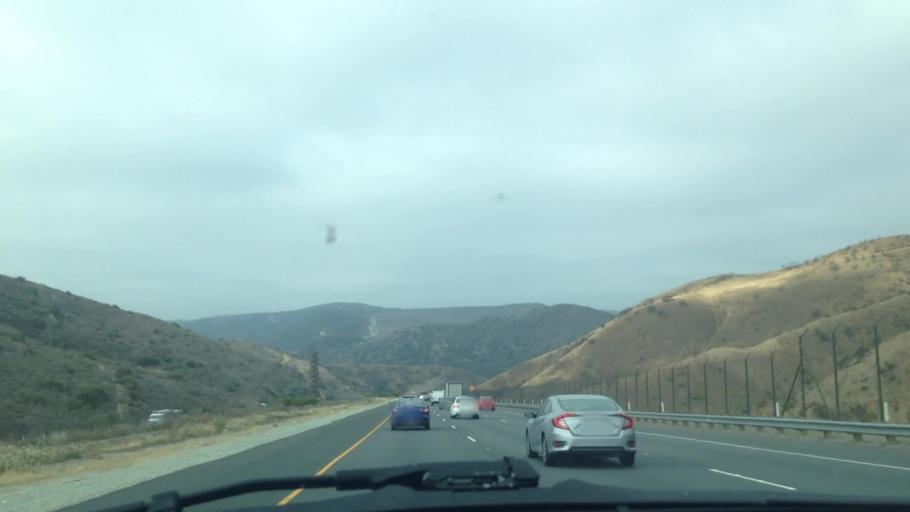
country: US
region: California
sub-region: Orange County
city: North Tustin
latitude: 33.8054
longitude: -117.7250
